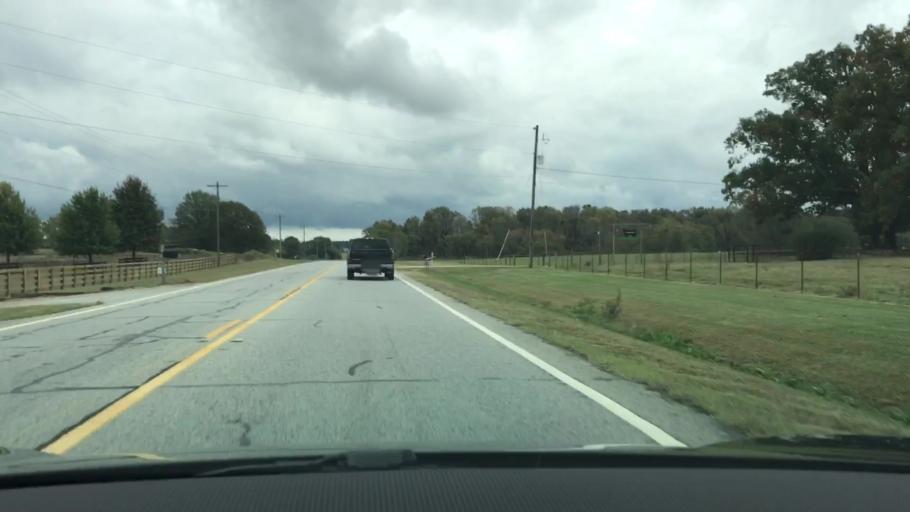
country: US
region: Georgia
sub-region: Oconee County
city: Watkinsville
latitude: 33.8259
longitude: -83.3722
